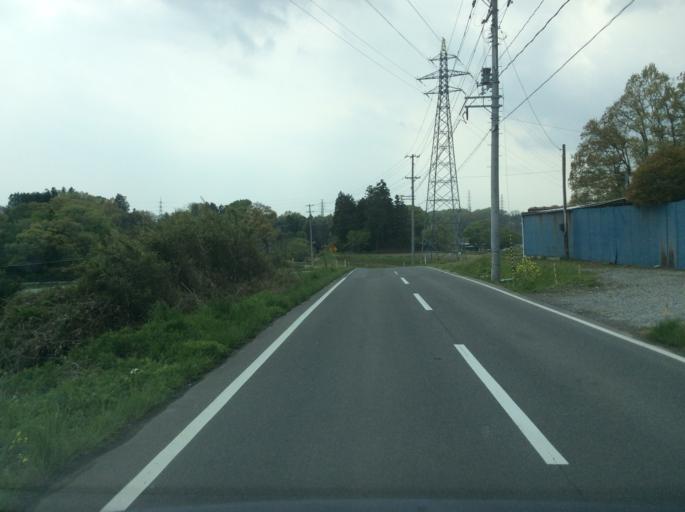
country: JP
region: Fukushima
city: Koriyama
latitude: 37.3860
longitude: 140.4259
